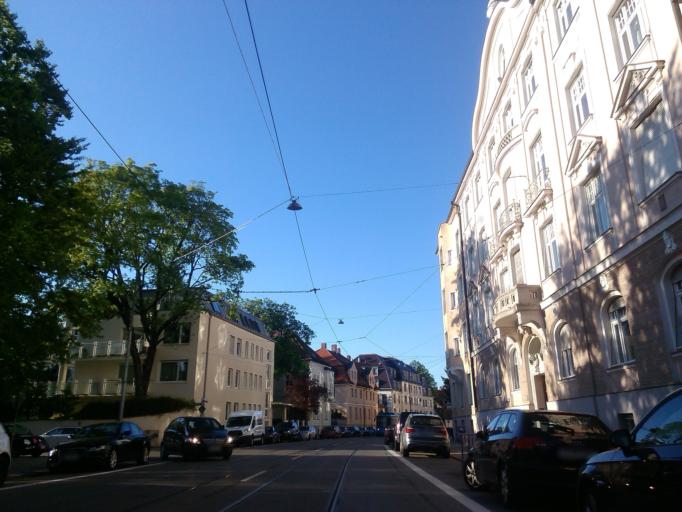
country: DE
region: Bavaria
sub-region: Upper Bavaria
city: Bogenhausen
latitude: 48.1433
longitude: 11.6014
